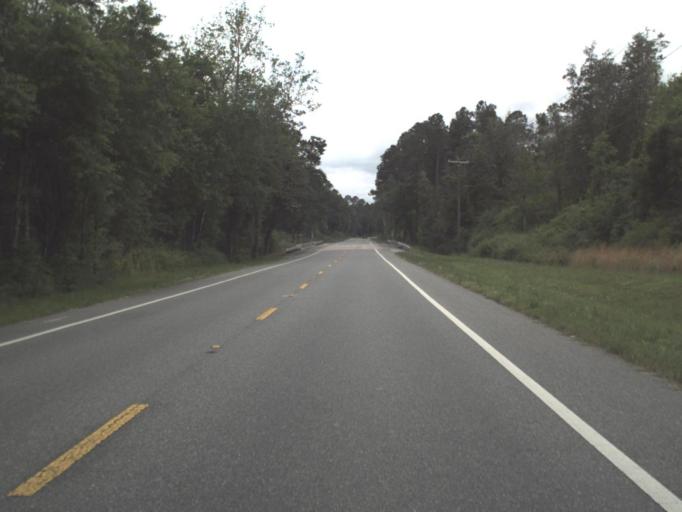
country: US
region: Florida
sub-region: Santa Rosa County
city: Point Baker
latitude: 30.8036
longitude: -87.0426
